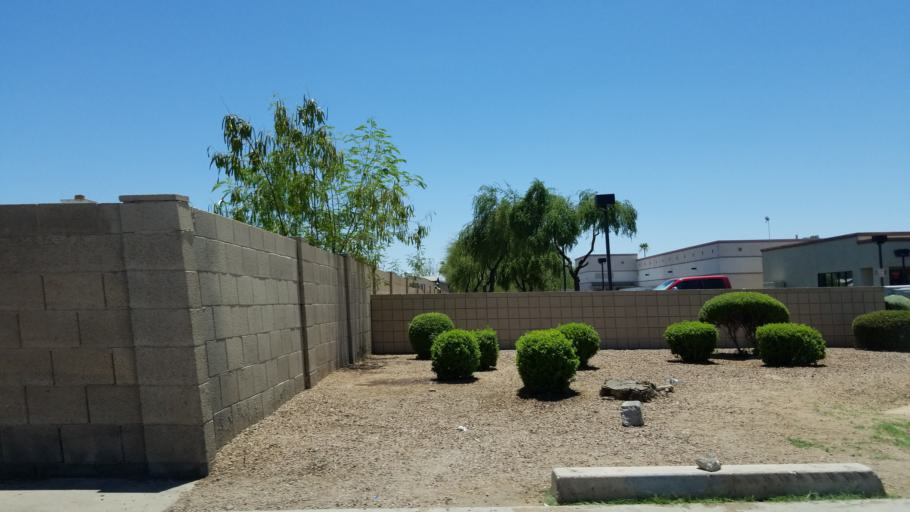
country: US
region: Arizona
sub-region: Maricopa County
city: Glendale
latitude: 33.5087
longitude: -112.2355
